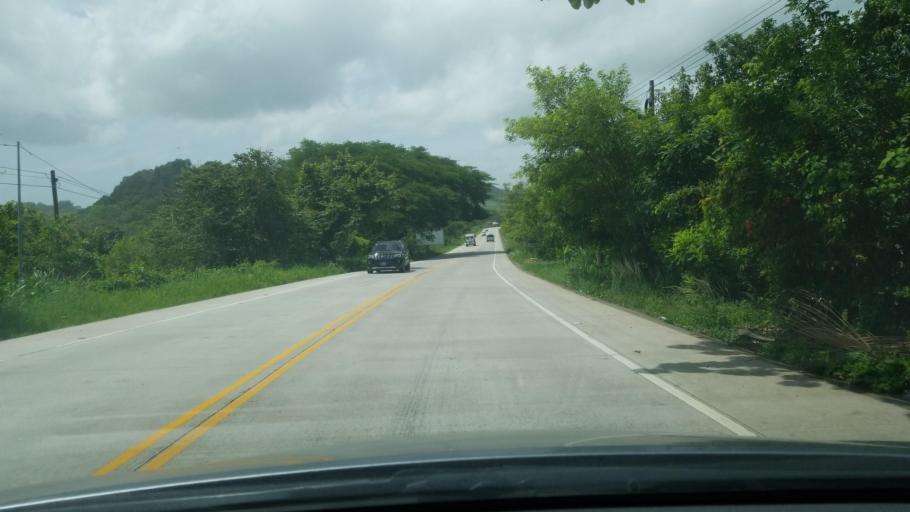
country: HN
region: Copan
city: Trinidad de Copan
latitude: 14.9613
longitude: -88.7723
